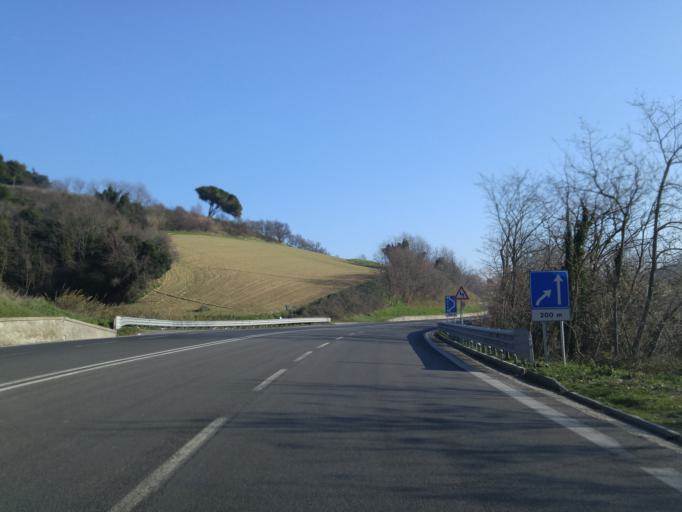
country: IT
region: The Marches
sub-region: Provincia di Pesaro e Urbino
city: Gradara
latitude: 43.9463
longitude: 12.8174
